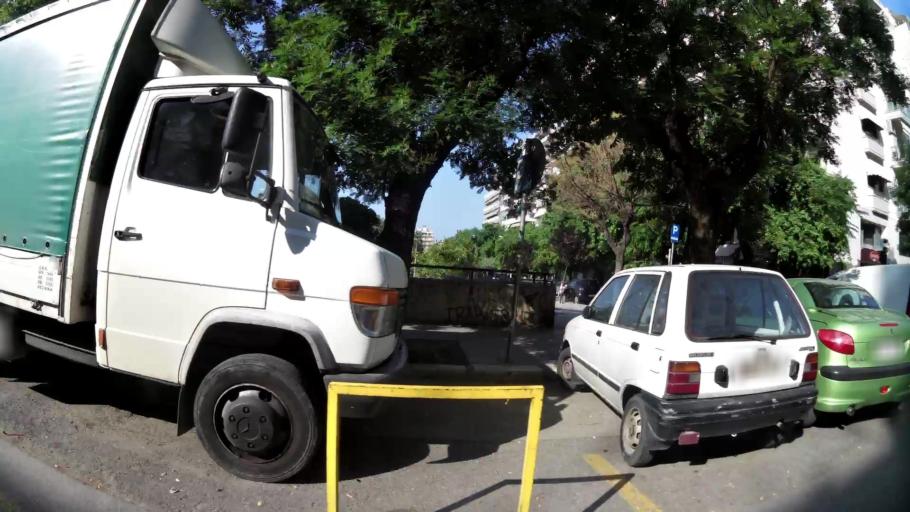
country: GR
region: Central Macedonia
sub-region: Nomos Thessalonikis
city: Sykies
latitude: 40.6386
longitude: 22.9456
